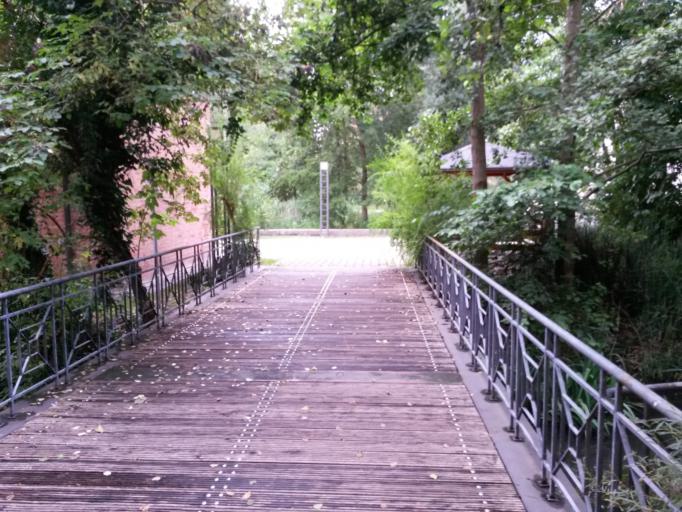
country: DE
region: Brandenburg
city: Eberswalde
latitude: 52.8330
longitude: 13.8182
